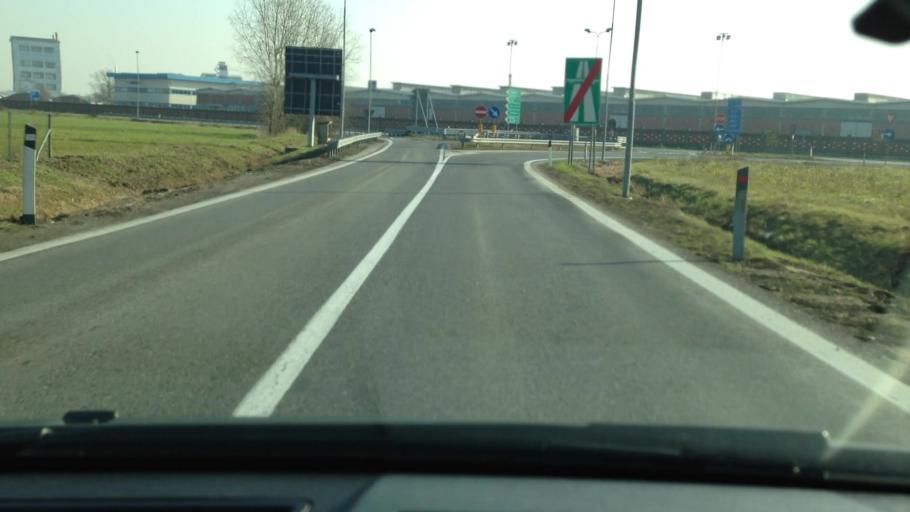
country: IT
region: Piedmont
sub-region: Provincia di Alessandria
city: Quattordio
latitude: 44.9004
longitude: 8.4200
